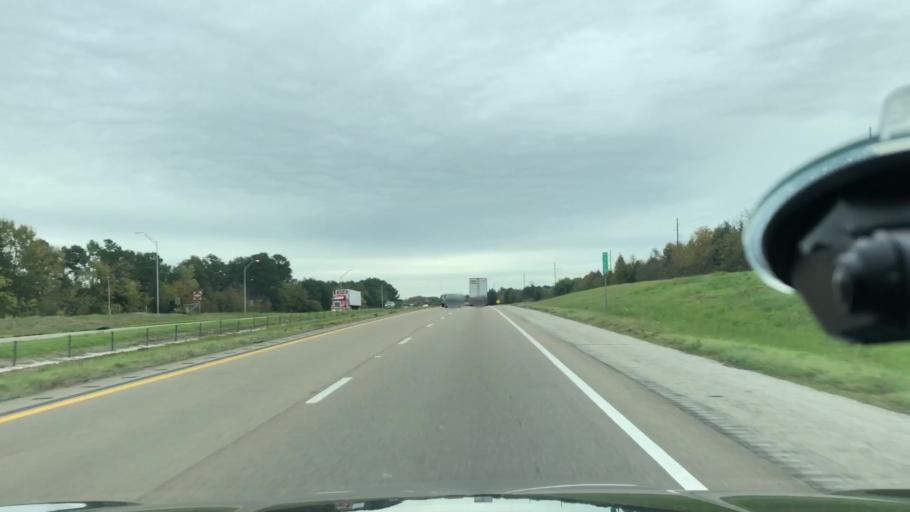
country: US
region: Texas
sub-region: Titus County
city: Mount Pleasant
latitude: 33.1583
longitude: -95.0431
